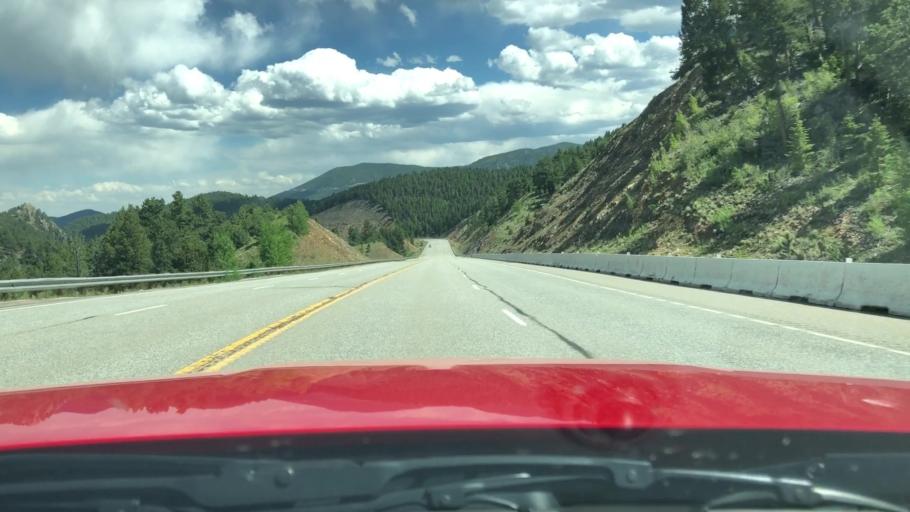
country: US
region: Colorado
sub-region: Gilpin County
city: Central City
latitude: 39.7754
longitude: -105.4738
